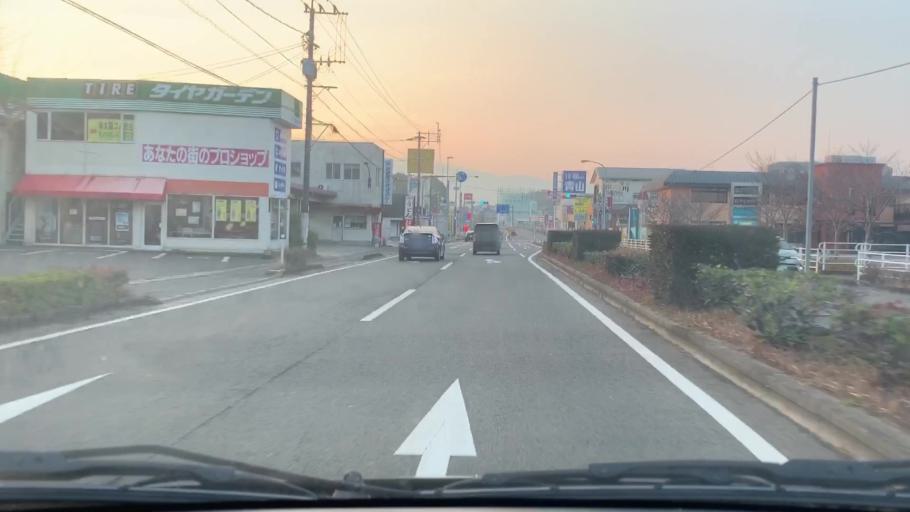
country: JP
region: Saga Prefecture
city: Imaricho-ko
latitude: 33.2694
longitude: 129.8737
